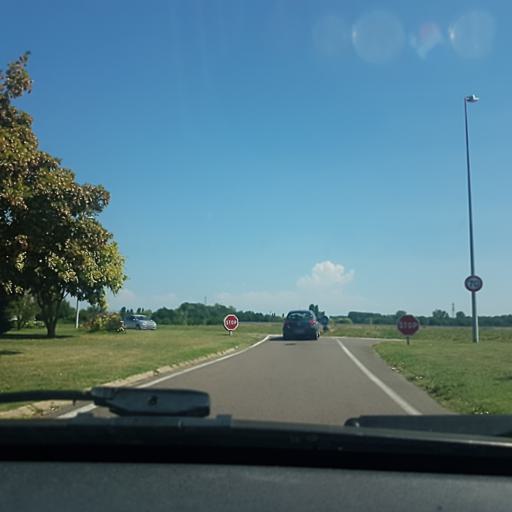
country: FR
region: Bourgogne
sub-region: Departement de Saone-et-Loire
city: Saint-Marcel
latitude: 46.7779
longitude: 4.8721
